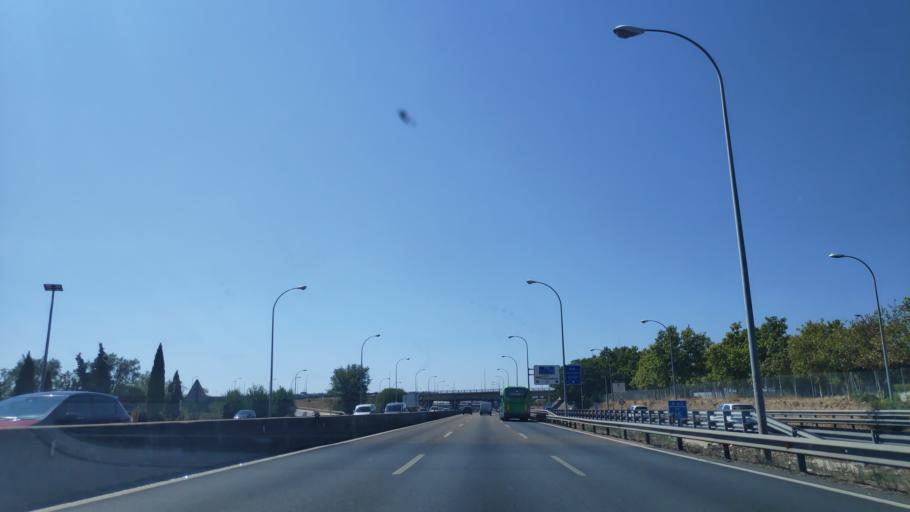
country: ES
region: Madrid
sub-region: Provincia de Madrid
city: Getafe
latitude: 40.2827
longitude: -3.7463
